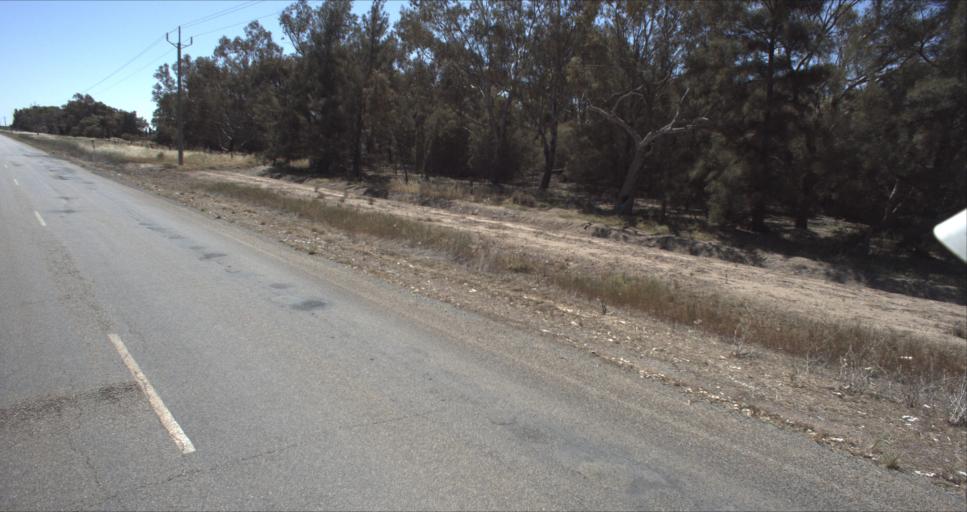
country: AU
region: New South Wales
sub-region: Leeton
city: Leeton
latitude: -34.4710
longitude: 146.2924
